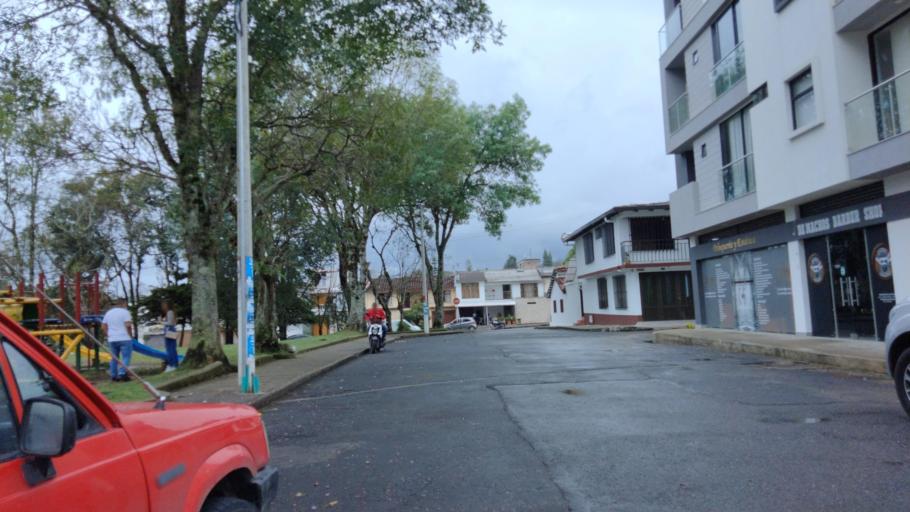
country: CO
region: Cauca
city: Popayan
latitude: 2.4588
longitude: -76.5900
